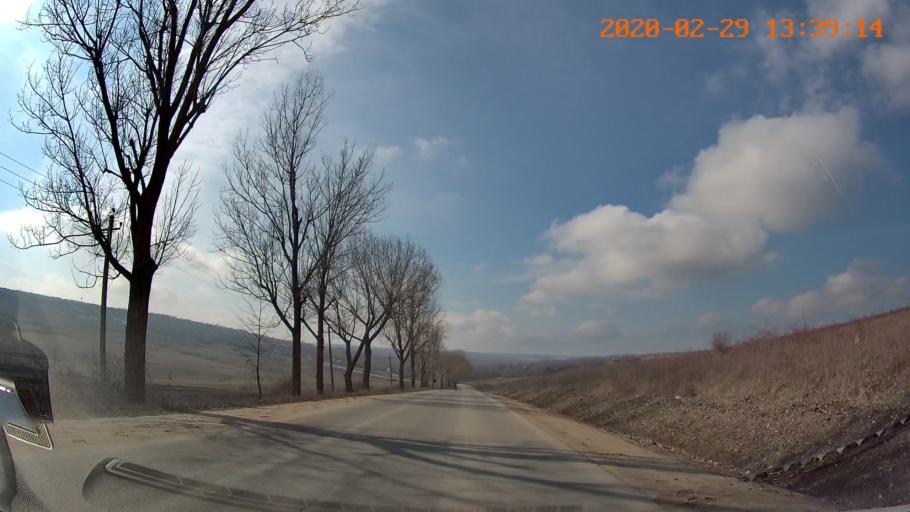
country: MD
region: Floresti
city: Leninskiy
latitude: 47.8515
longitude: 28.5847
